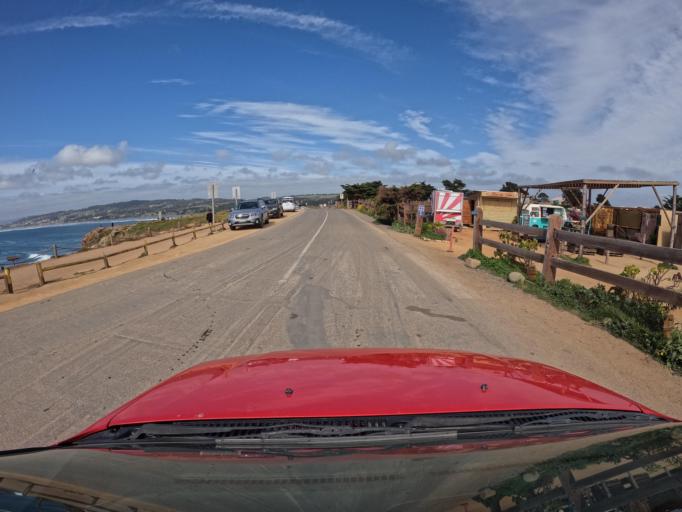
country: CL
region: O'Higgins
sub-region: Provincia de Colchagua
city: Santa Cruz
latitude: -34.4256
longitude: -72.0475
